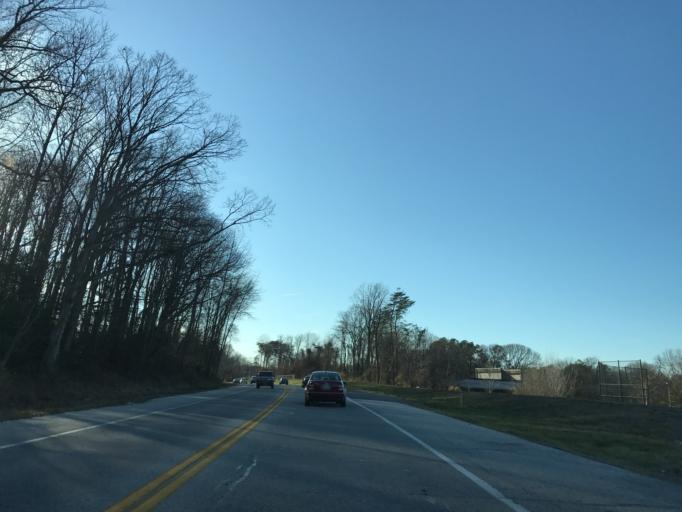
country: US
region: Maryland
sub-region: Anne Arundel County
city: Cape Saint Claire
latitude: 39.0357
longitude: -76.4526
